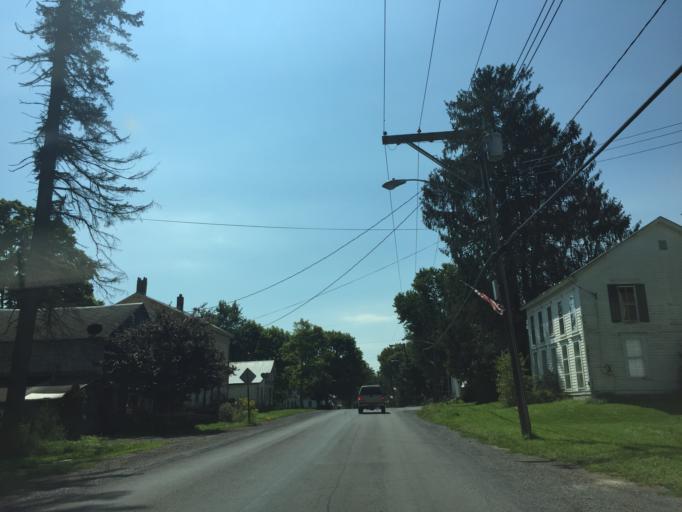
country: US
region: New York
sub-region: Otsego County
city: Worcester
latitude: 42.6506
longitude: -74.7970
